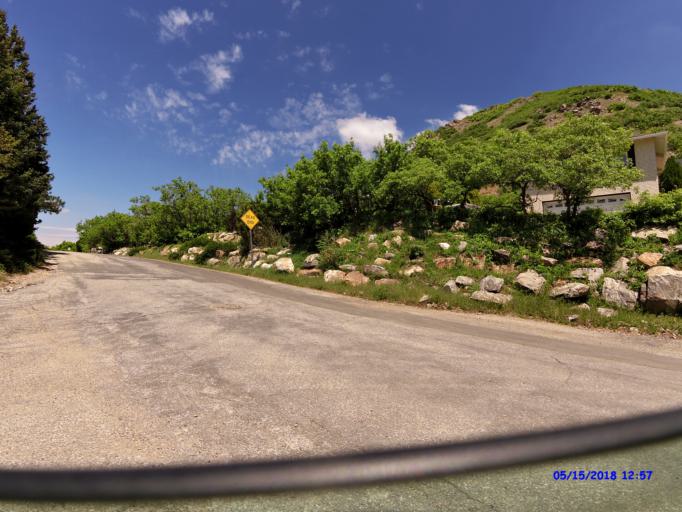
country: US
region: Utah
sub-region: Weber County
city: Uintah
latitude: 41.1639
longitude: -111.9195
